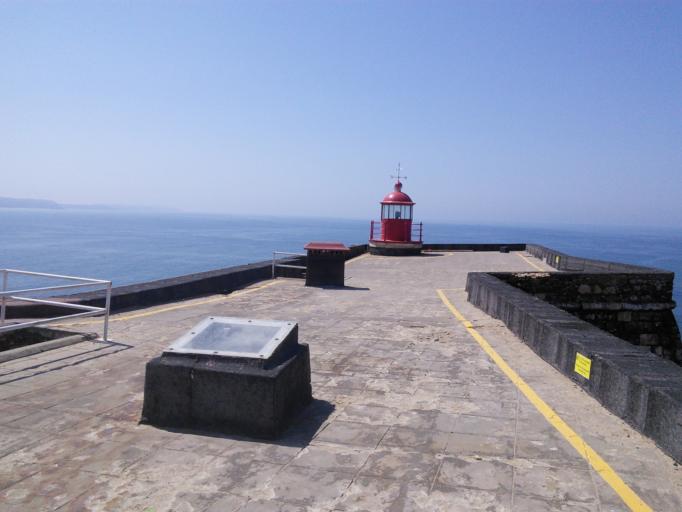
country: PT
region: Leiria
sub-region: Nazare
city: Nazare
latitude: 39.6047
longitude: -9.0849
